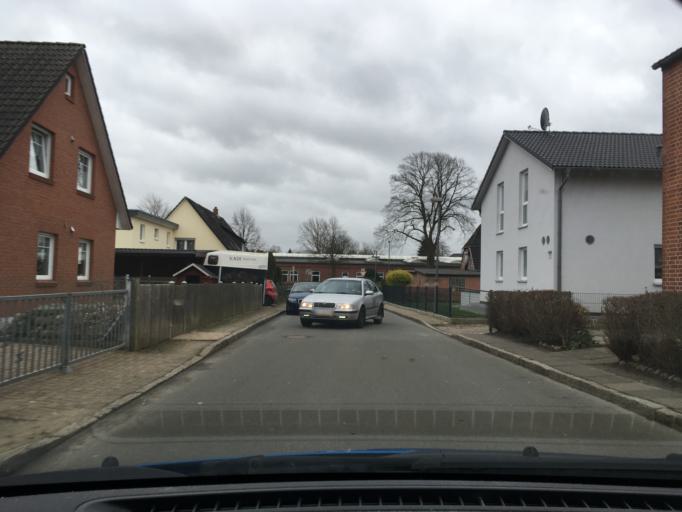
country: DE
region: Schleswig-Holstein
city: Lauenburg
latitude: 53.3791
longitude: 10.5500
